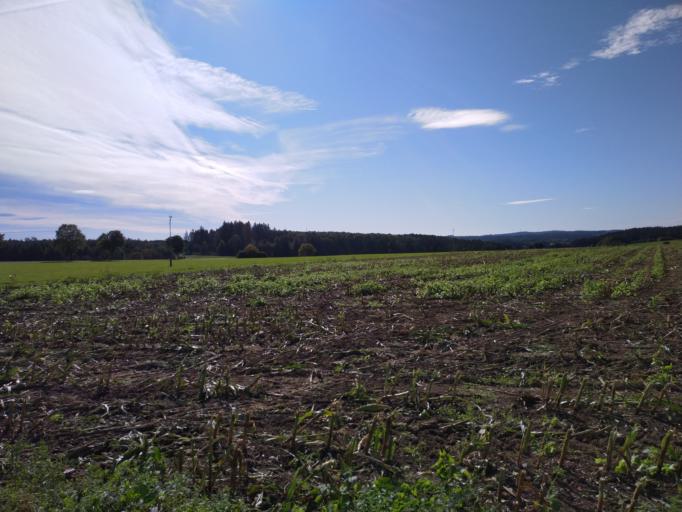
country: DE
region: Bavaria
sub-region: Swabia
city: Irsee
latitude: 47.8881
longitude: 10.5730
